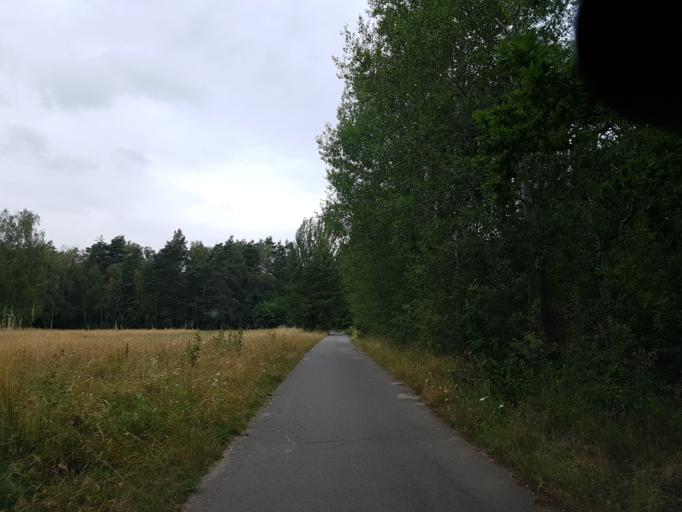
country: DE
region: Brandenburg
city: Sallgast
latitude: 51.5751
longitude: 13.8631
